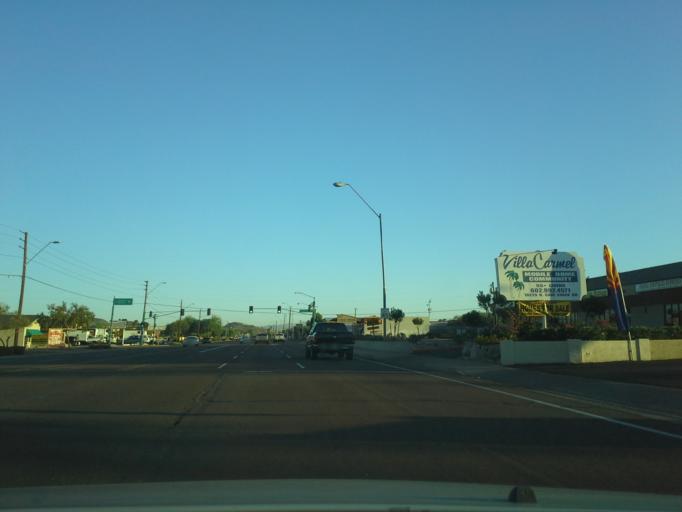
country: US
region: Arizona
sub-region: Maricopa County
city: Paradise Valley
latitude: 33.6340
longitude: -112.0307
